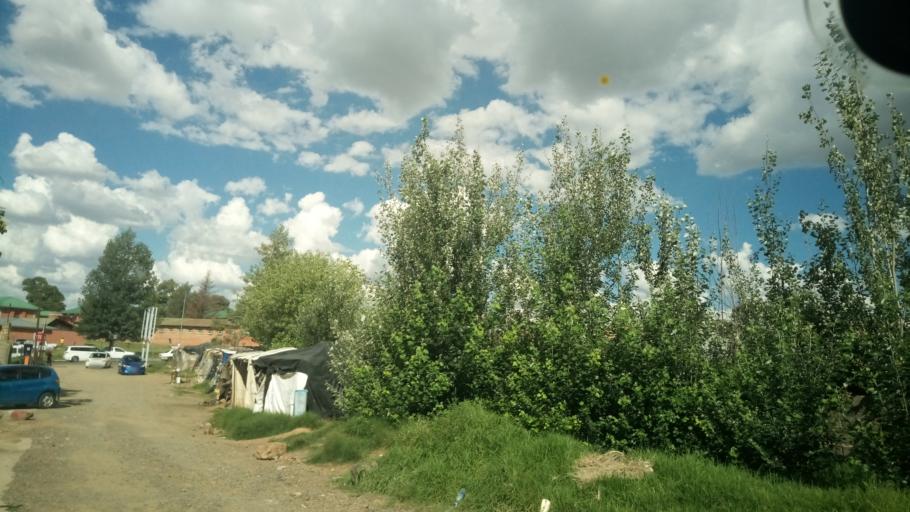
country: LS
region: Maseru
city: Maseru
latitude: -29.3037
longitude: 27.4819
